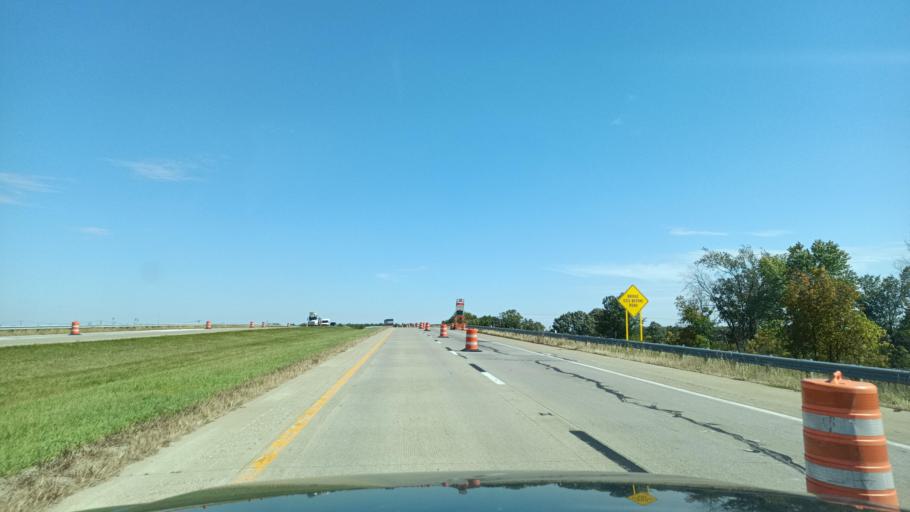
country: US
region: Ohio
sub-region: Defiance County
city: Defiance
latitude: 41.2610
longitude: -84.4421
